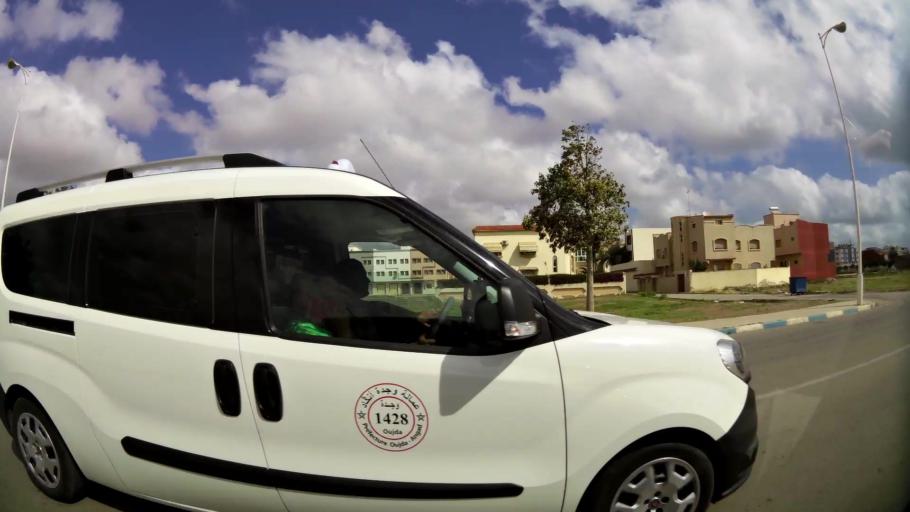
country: MA
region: Oriental
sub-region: Nador
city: Nador
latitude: 35.1642
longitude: -2.9205
